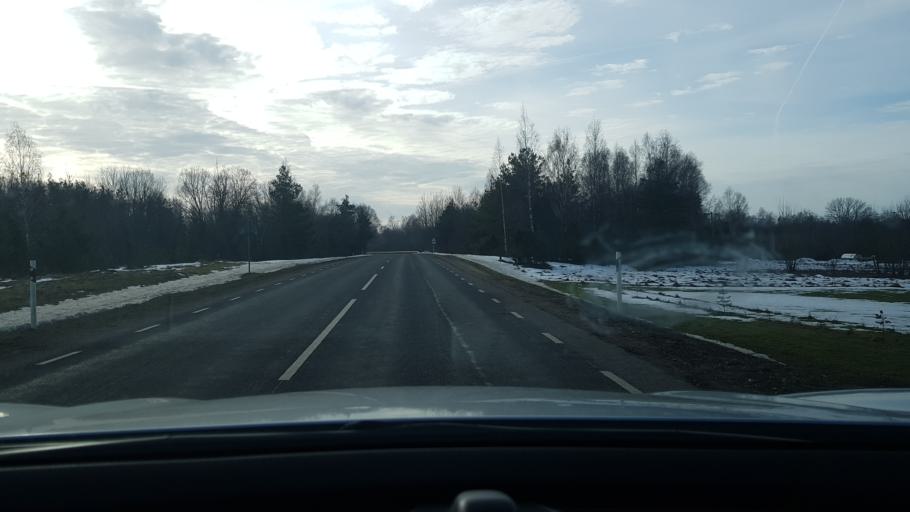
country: EE
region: Saare
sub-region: Kuressaare linn
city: Kuressaare
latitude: 58.3070
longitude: 22.5405
